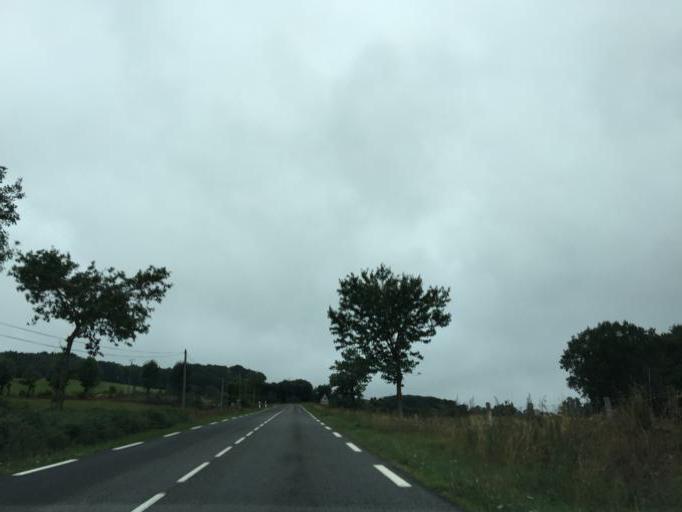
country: FR
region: Midi-Pyrenees
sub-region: Departement de l'Aveyron
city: Salles-Curan
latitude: 44.2417
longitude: 2.9050
